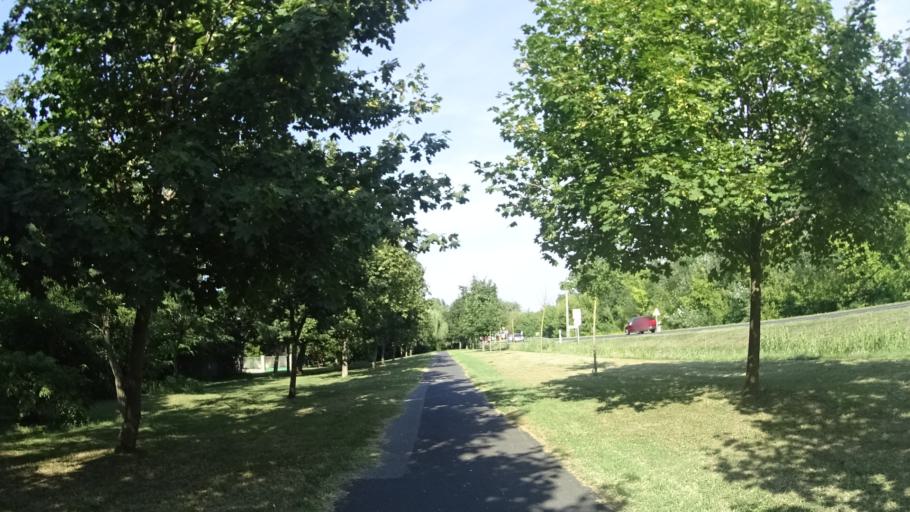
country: HU
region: Somogy
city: Balatonszarszo
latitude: 46.8171
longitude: 17.7934
